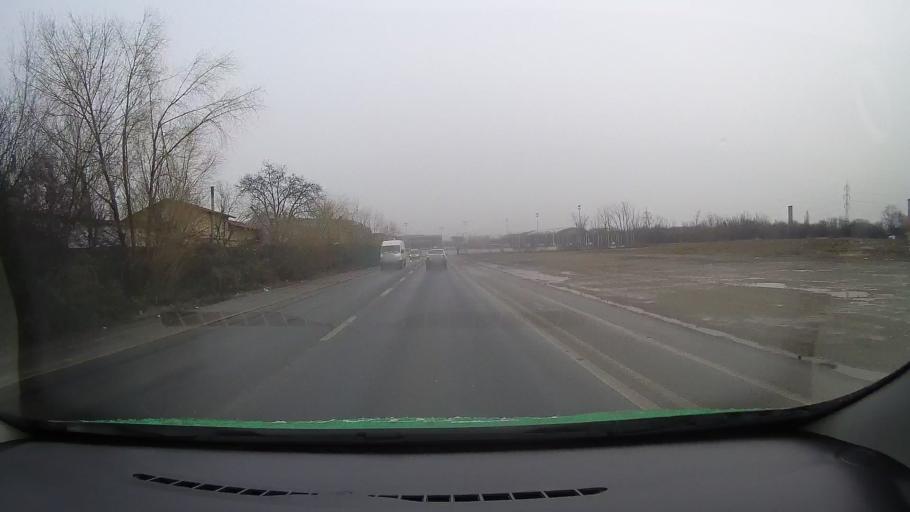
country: RO
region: Timis
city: Timisoara
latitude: 45.7399
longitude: 21.2499
